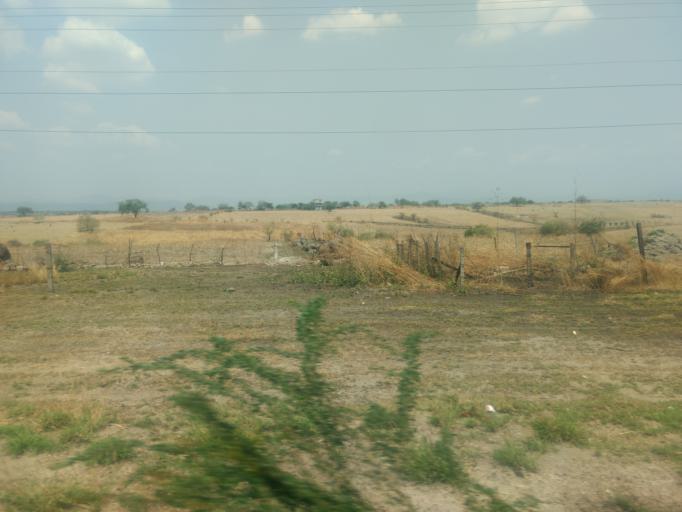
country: MX
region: Morelos
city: Ahuehuetzingo
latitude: 18.6970
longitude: -99.2797
